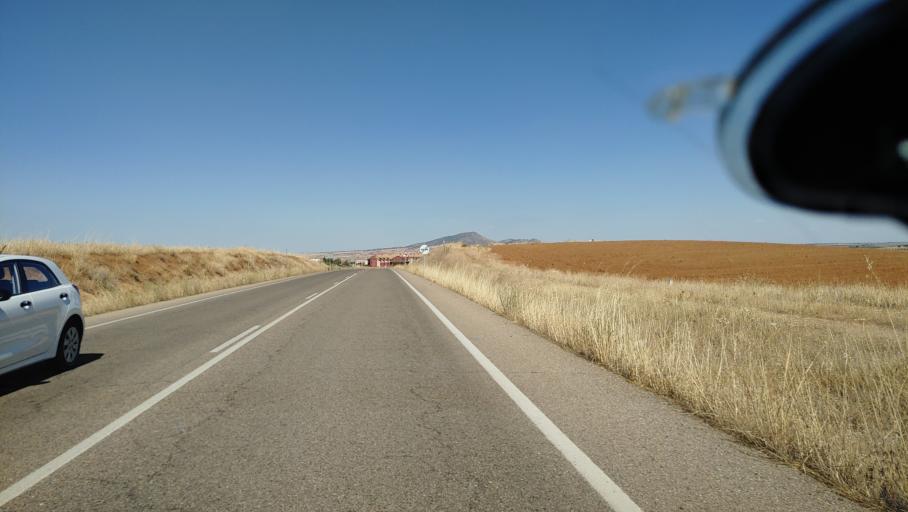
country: ES
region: Castille-La Mancha
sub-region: Province of Toledo
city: Pulgar
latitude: 39.6855
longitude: -4.1657
